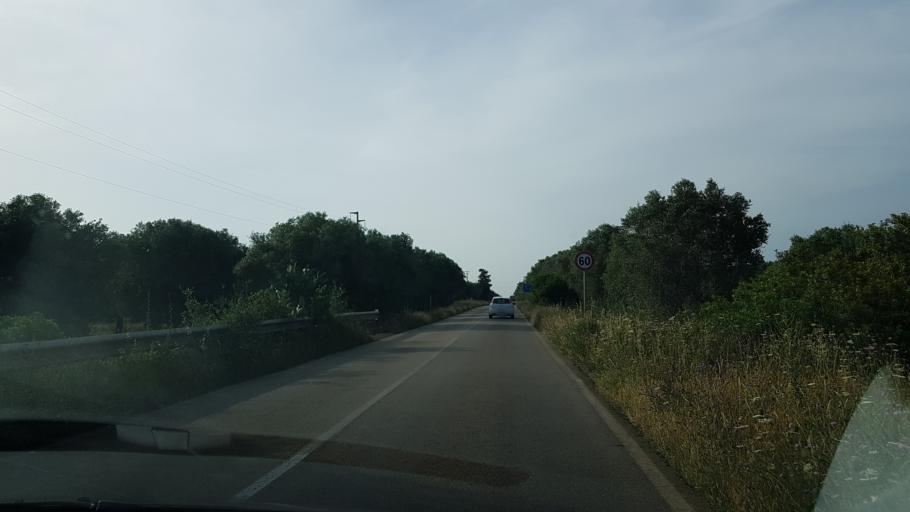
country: IT
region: Apulia
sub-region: Provincia di Brindisi
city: San Pancrazio Salentino
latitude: 40.3506
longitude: 17.8457
